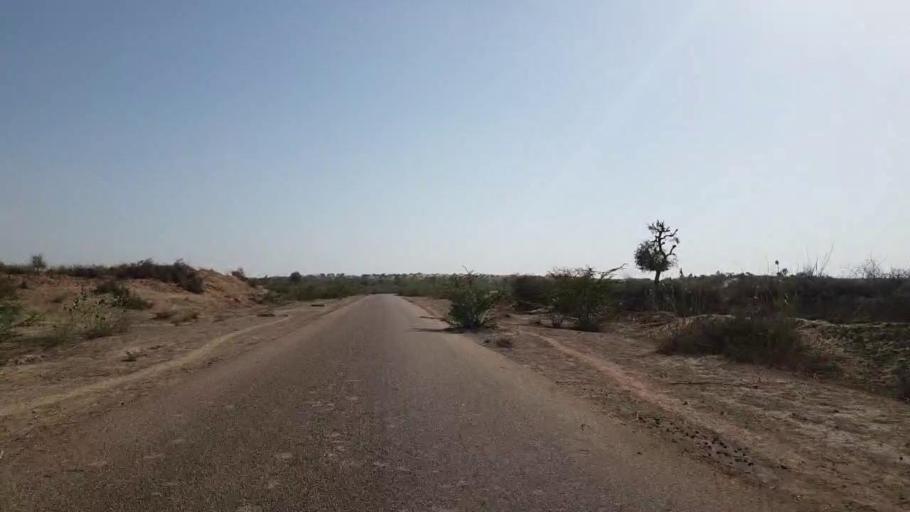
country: PK
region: Sindh
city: Islamkot
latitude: 25.0672
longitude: 70.0411
